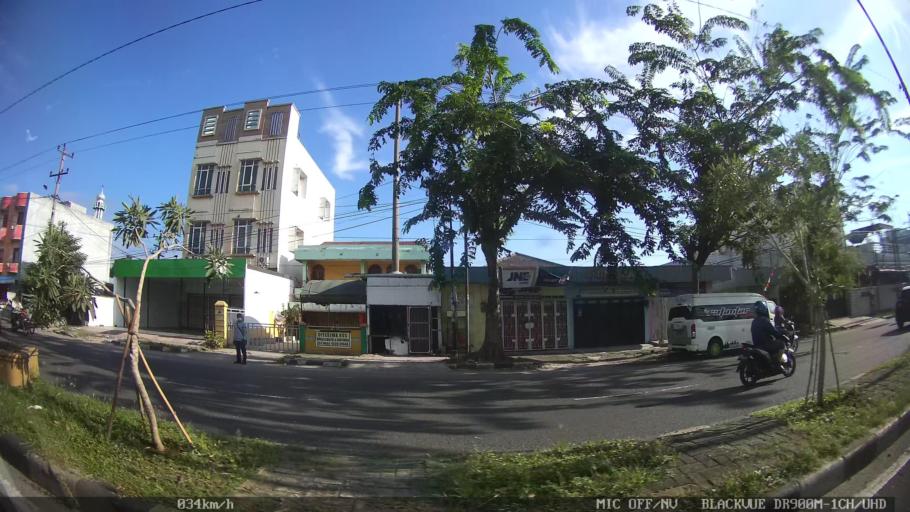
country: ID
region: North Sumatra
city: Sunggal
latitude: 3.5910
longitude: 98.6383
